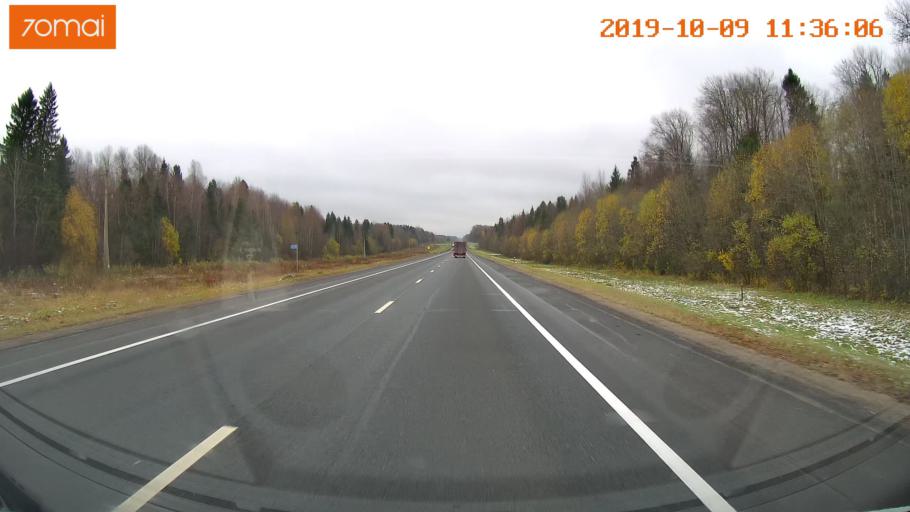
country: RU
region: Vologda
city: Gryazovets
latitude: 58.9952
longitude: 40.1329
